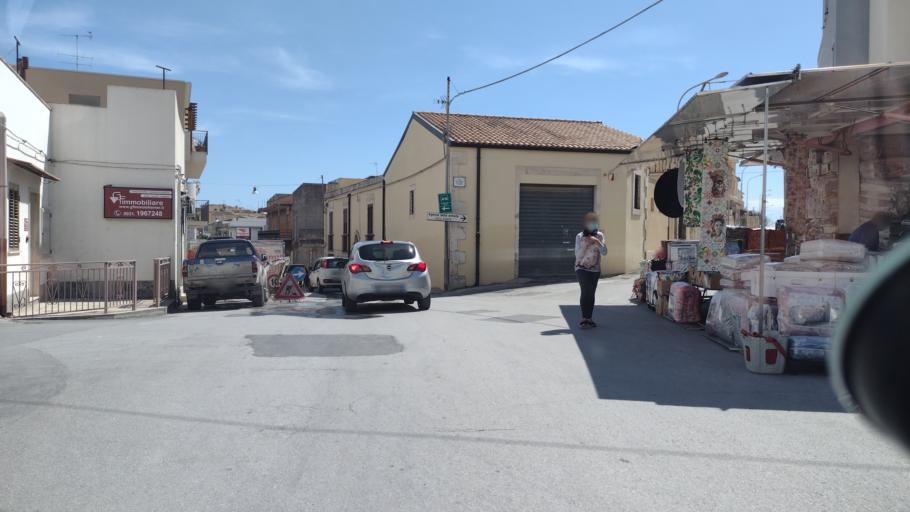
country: IT
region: Sicily
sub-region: Provincia di Siracusa
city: Noto
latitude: 36.8876
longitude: 15.0714
